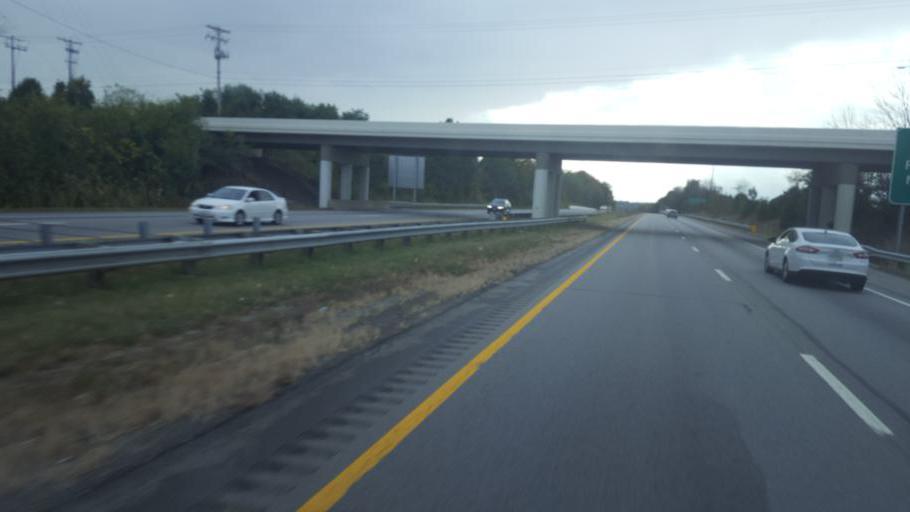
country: US
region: Ohio
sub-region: Medina County
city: Wadsworth
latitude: 41.0360
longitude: -81.7489
